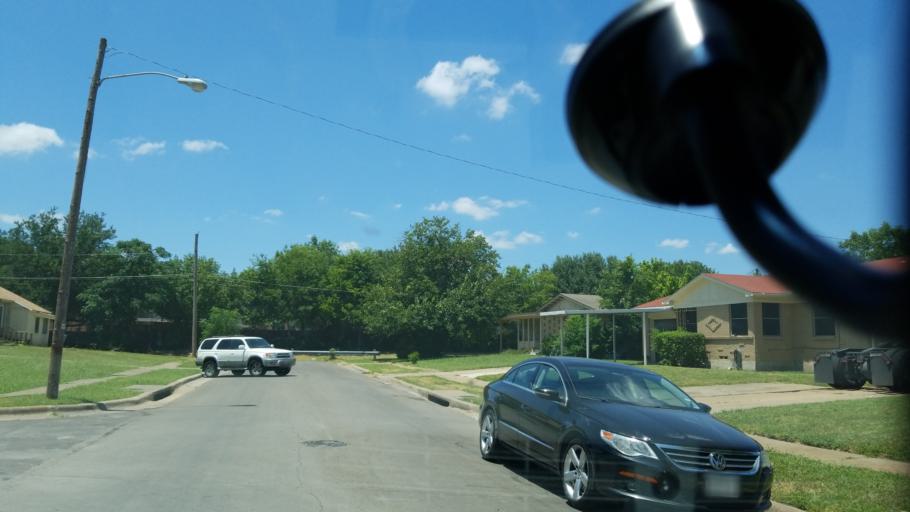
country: US
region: Texas
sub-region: Dallas County
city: Cockrell Hill
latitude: 32.6862
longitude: -96.8168
